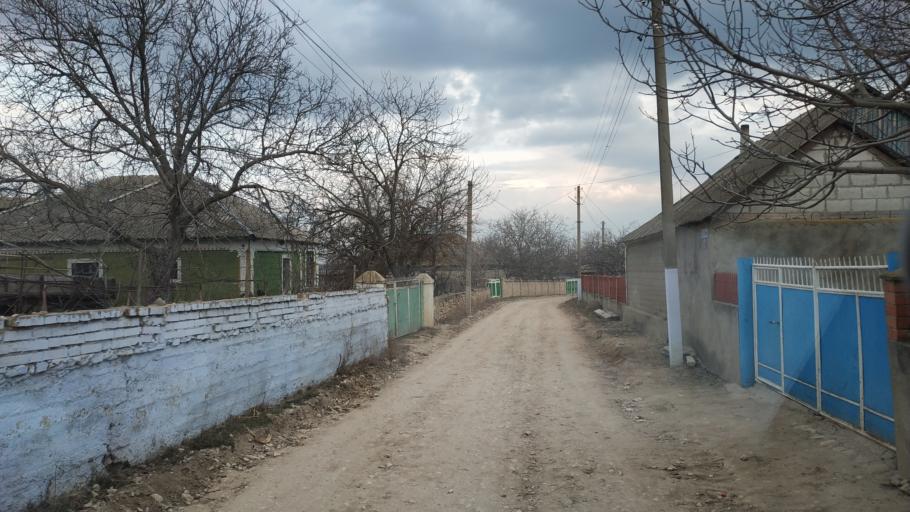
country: MD
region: Telenesti
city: Grigoriopol
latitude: 47.0227
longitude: 29.3518
